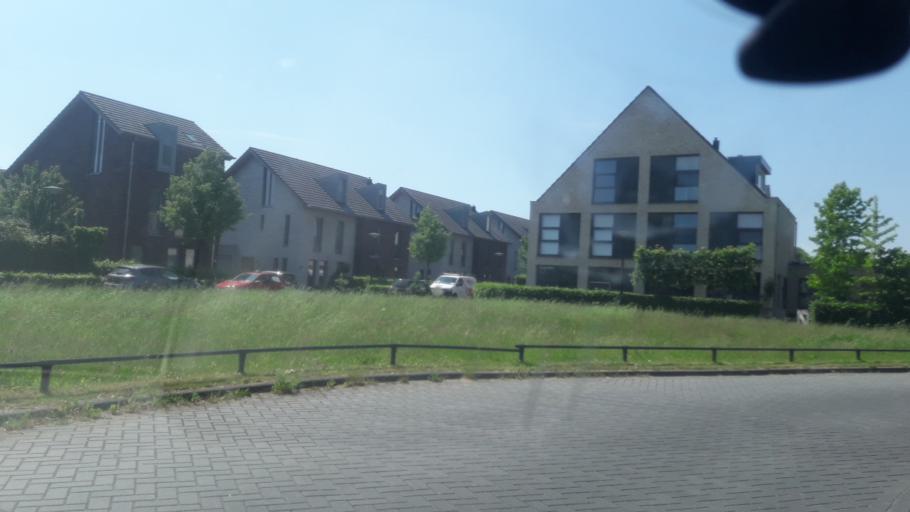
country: NL
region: Overijssel
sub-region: Gemeente Deventer
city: Schalkhaar
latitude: 52.2634
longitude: 6.2327
